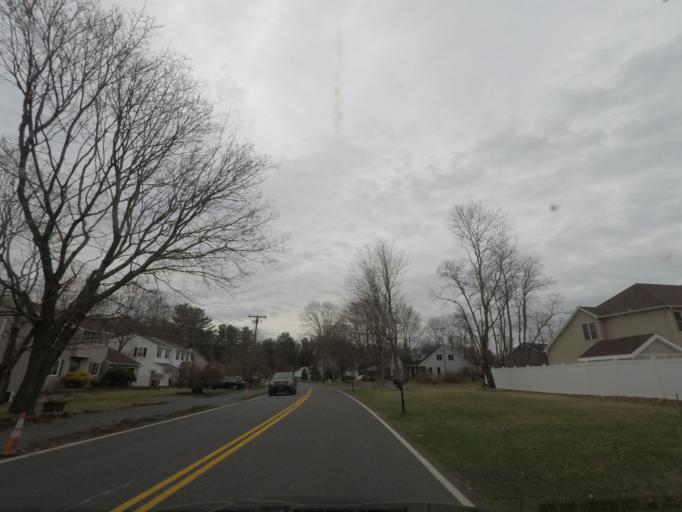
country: US
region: New York
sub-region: Albany County
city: Delmar
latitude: 42.6036
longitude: -73.8323
